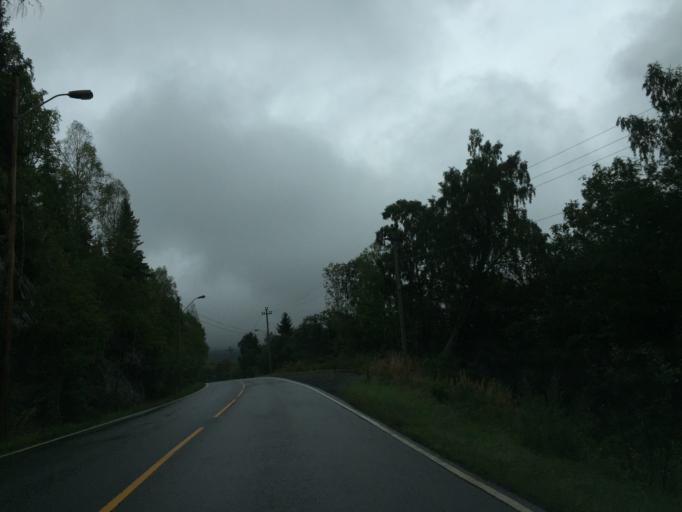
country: NO
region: Akershus
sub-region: Baerum
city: Lysaker
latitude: 60.0094
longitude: 10.6143
